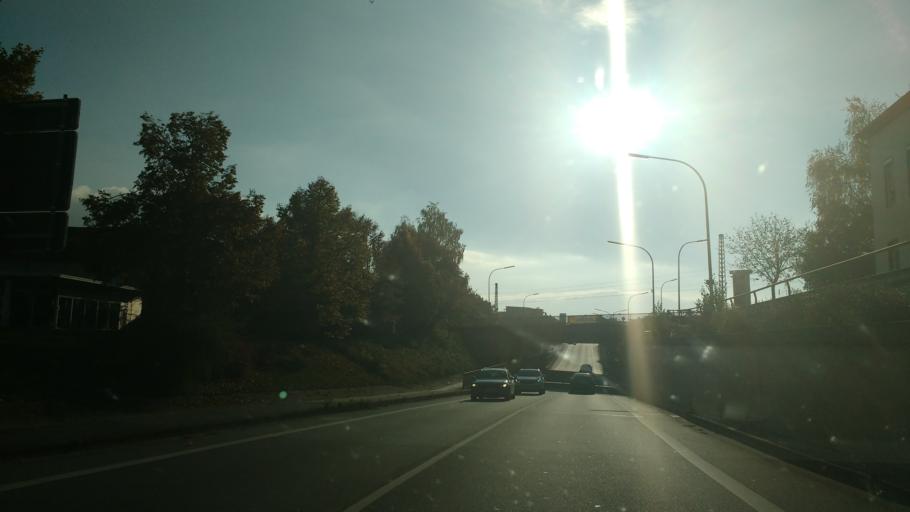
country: DE
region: Rheinland-Pfalz
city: Worms
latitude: 49.6233
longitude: 8.3556
